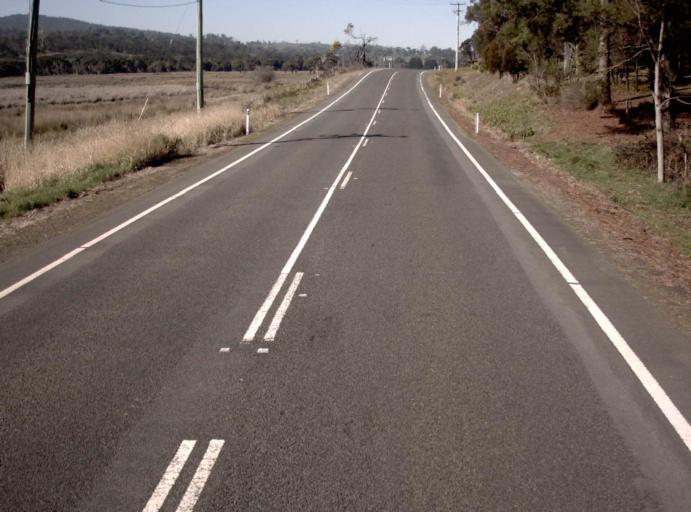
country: AU
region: Tasmania
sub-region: Launceston
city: Mayfield
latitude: -41.3178
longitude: 147.0567
